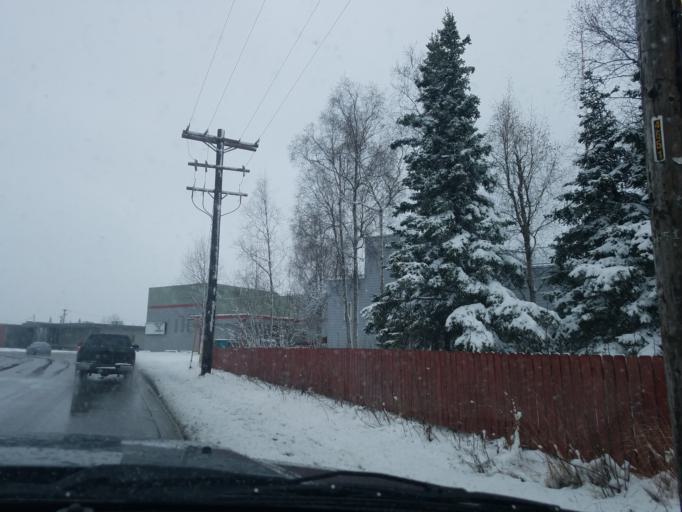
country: US
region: Alaska
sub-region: Anchorage Municipality
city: Anchorage
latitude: 61.1918
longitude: -149.9060
